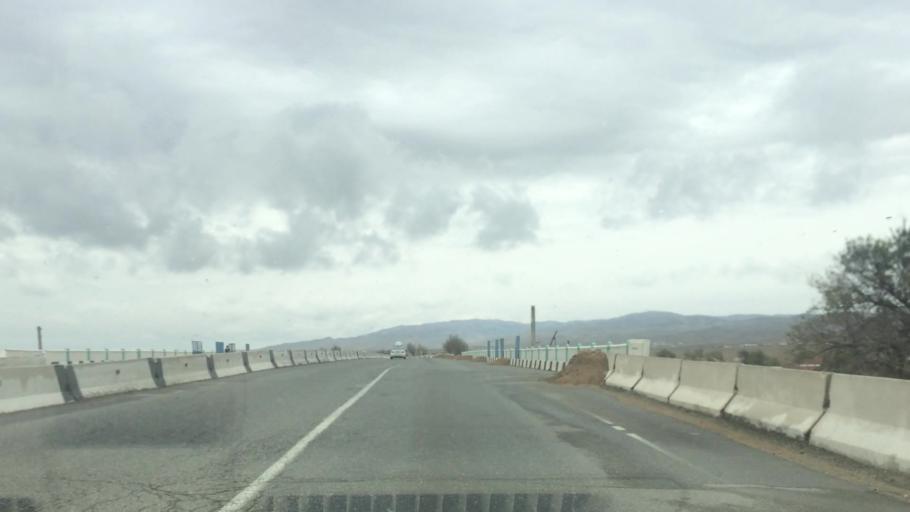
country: UZ
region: Samarqand
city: Bulung'ur
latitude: 39.8374
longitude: 67.4373
